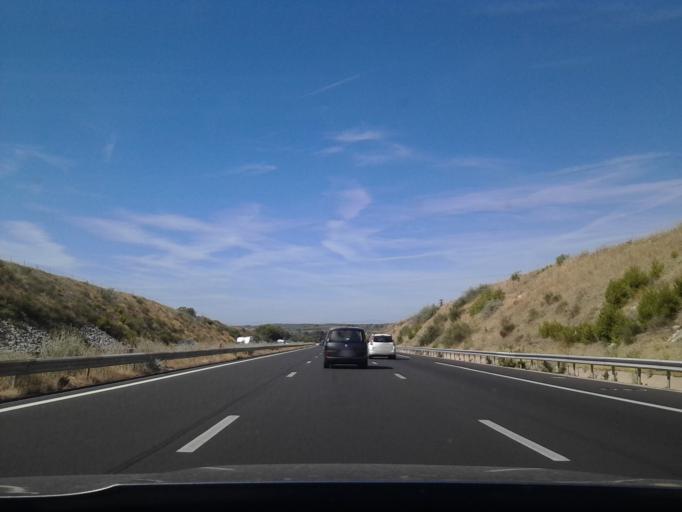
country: FR
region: Languedoc-Roussillon
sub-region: Departement de l'Herault
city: Lespignan
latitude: 43.2592
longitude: 3.1669
